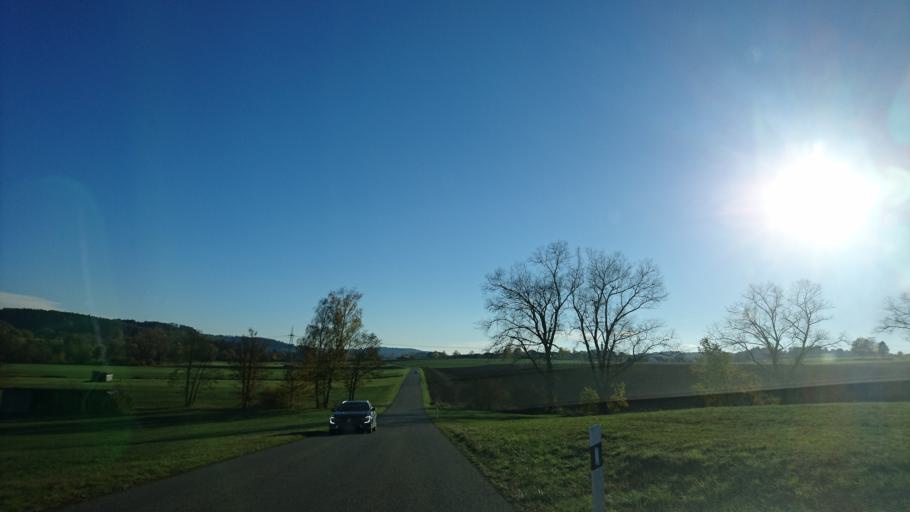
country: DE
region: Bavaria
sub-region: Swabia
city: Zusmarshausen
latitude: 48.3906
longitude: 10.5774
